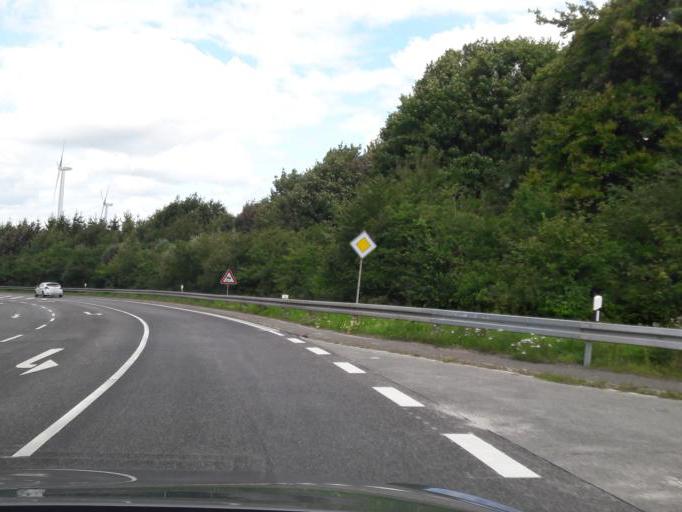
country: DE
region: Rheinland-Pfalz
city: Eckersweiler
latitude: 49.5602
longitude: 7.2724
